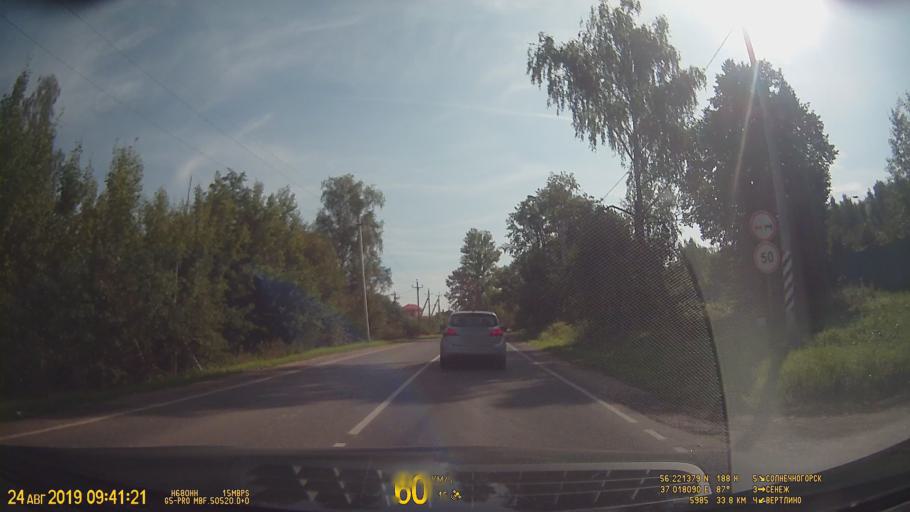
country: RU
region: Moskovskaya
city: Solnechnogorsk
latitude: 56.2214
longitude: 37.0185
